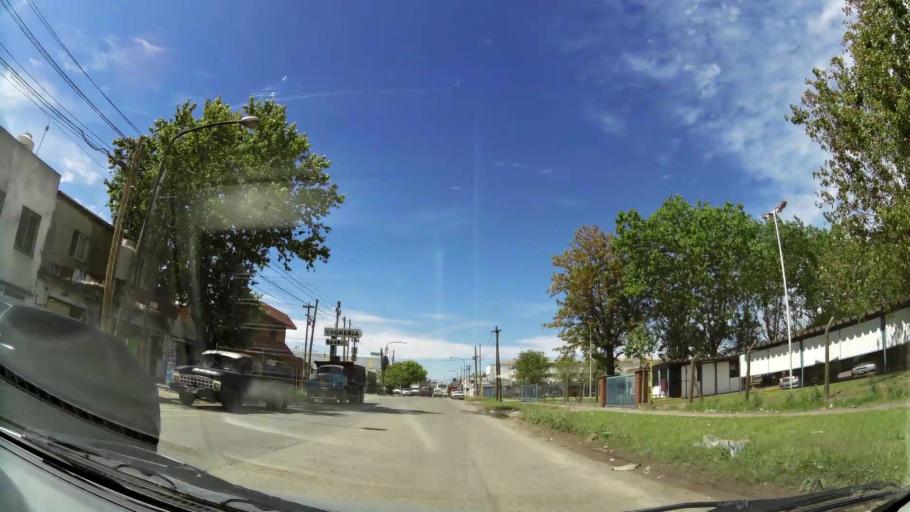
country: AR
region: Buenos Aires
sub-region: Partido de Quilmes
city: Quilmes
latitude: -34.7494
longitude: -58.3030
